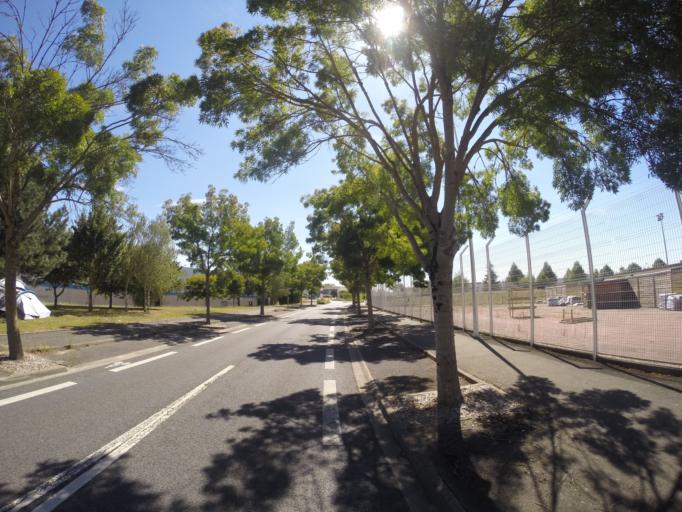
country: FR
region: Centre
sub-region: Departement d'Indre-et-Loire
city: Chanceaux-sur-Choisille
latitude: 47.4277
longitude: 0.7065
